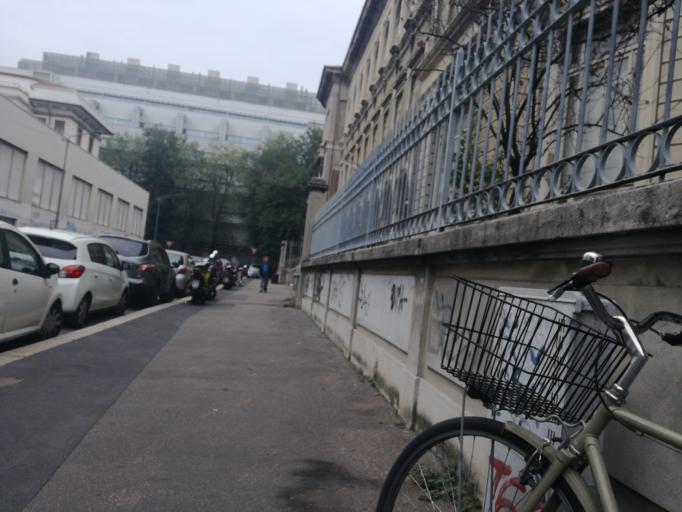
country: IT
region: Lombardy
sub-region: Citta metropolitana di Milano
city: Milano
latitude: 45.4736
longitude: 9.2274
